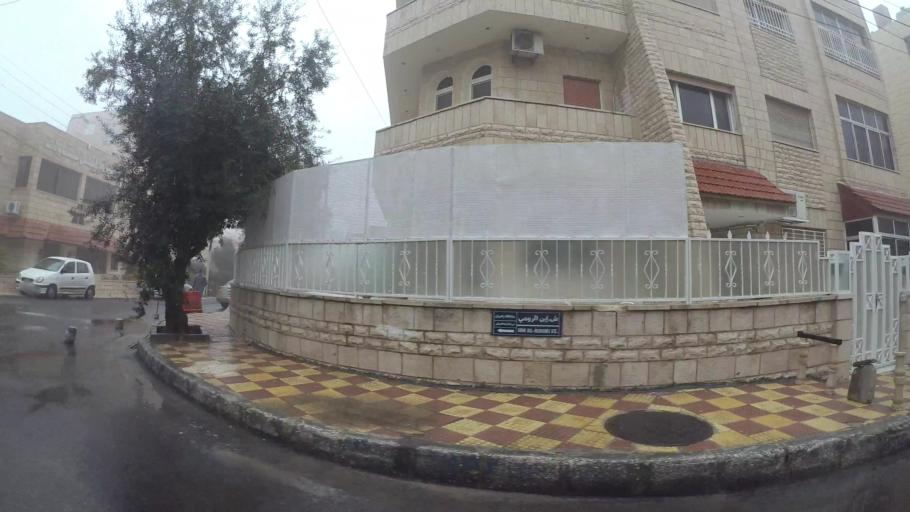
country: JO
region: Amman
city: Wadi as Sir
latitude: 31.9629
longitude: 35.8716
